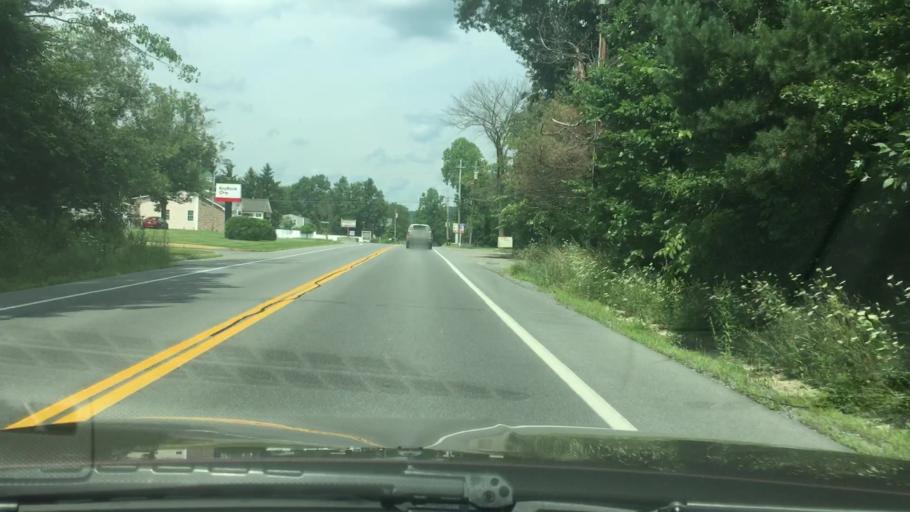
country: US
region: New York
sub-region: Dutchess County
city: Pawling
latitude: 41.6228
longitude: -73.6842
